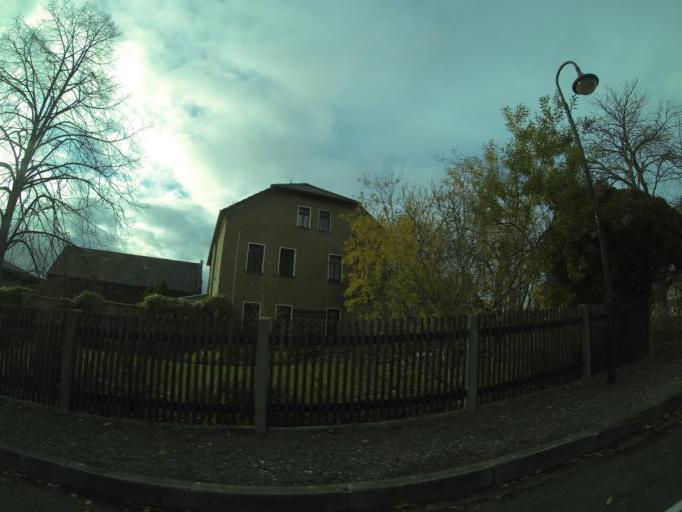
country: DE
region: Thuringia
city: Schmolln
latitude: 50.8772
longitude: 12.3771
